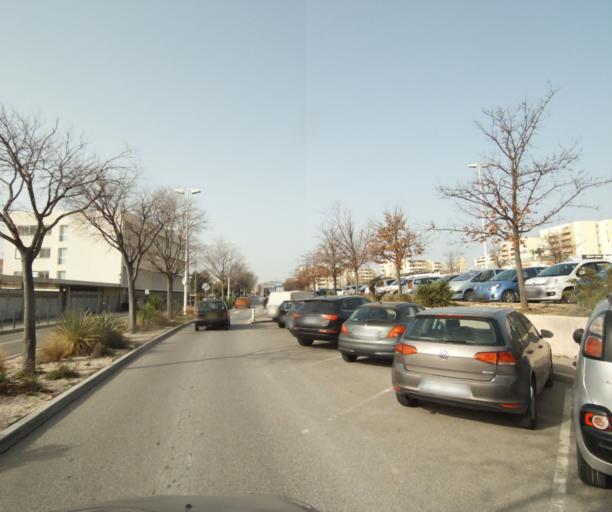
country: FR
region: Provence-Alpes-Cote d'Azur
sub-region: Departement des Bouches-du-Rhone
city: Vitrolles
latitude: 43.4470
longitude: 5.2476
